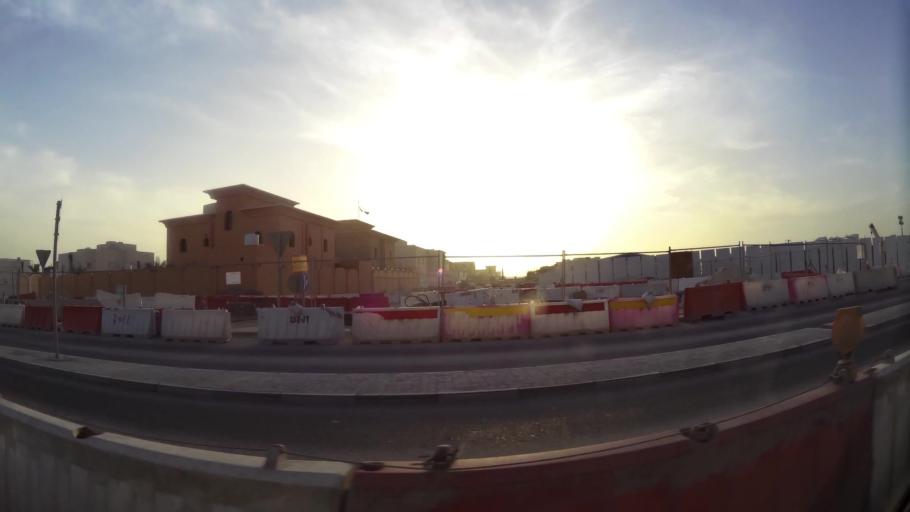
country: QA
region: Al Wakrah
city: Al Wakrah
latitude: 25.1631
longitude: 51.5902
